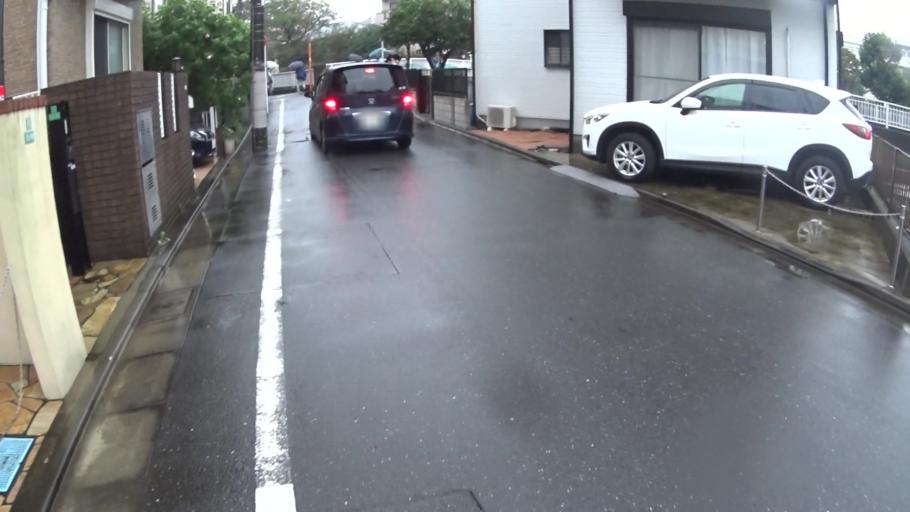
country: JP
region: Saitama
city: Wako
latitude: 35.7449
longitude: 139.6517
